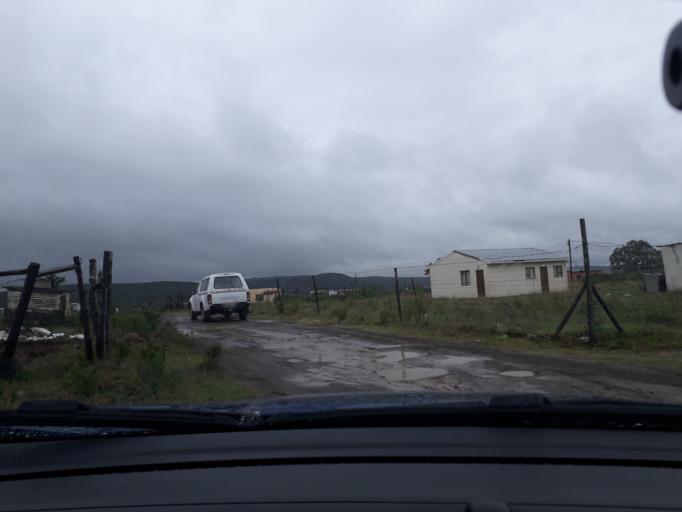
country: ZA
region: Eastern Cape
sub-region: Buffalo City Metropolitan Municipality
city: Bhisho
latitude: -32.8086
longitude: 27.3642
